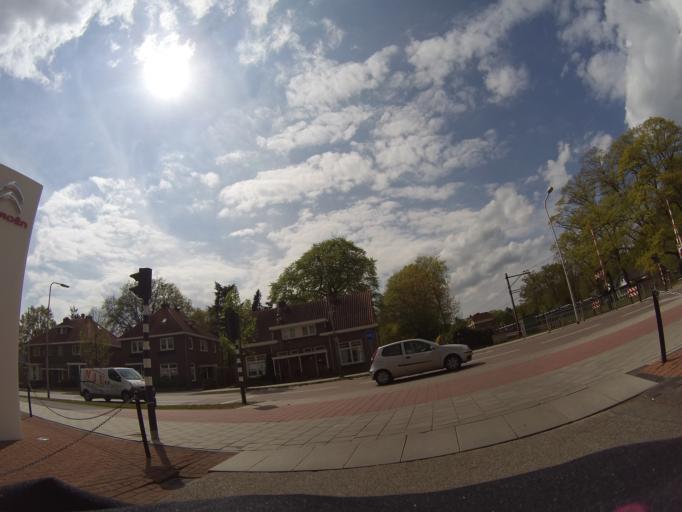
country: NL
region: Overijssel
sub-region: Gemeente Twenterand
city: Den Ham
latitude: 52.5098
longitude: 6.4198
